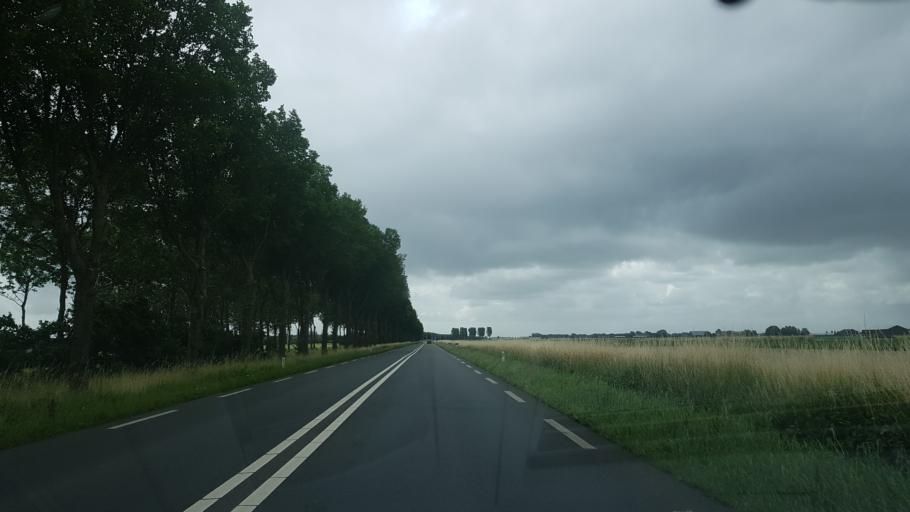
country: NL
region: North Holland
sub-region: Gemeente Medemblik
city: Medemblik
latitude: 52.7546
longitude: 5.0973
